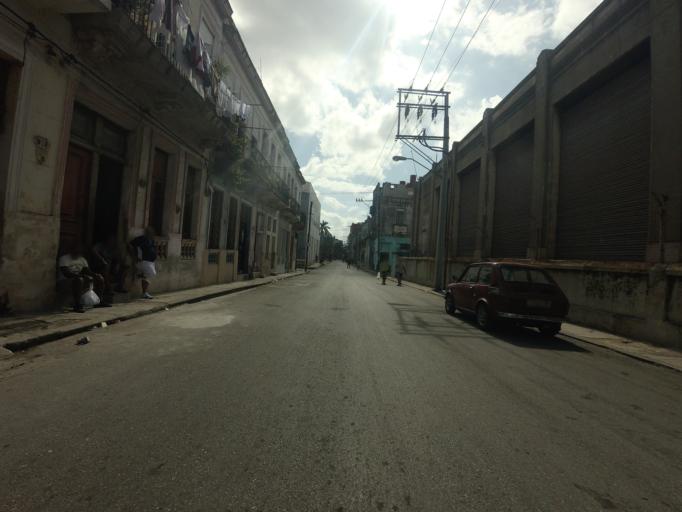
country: CU
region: La Habana
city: Havana
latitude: 23.1328
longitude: -82.3764
